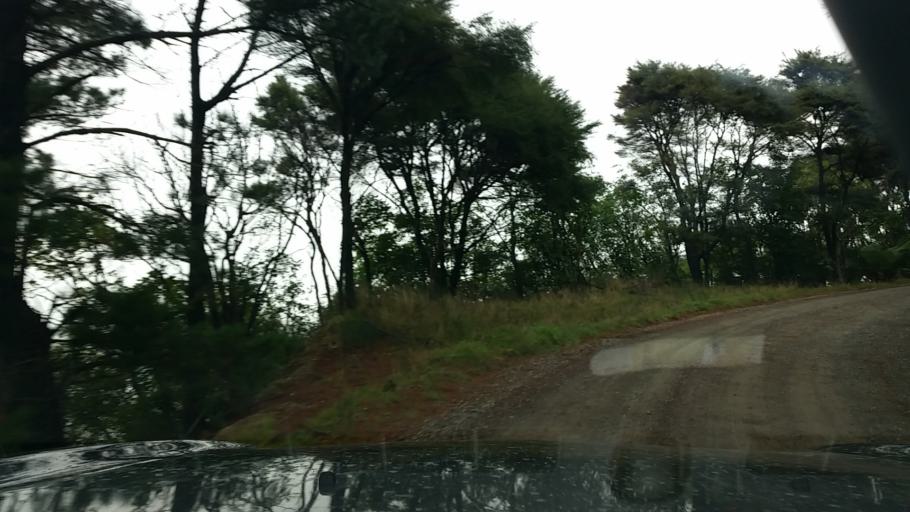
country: NZ
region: Marlborough
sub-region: Marlborough District
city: Picton
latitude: -41.1691
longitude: 174.0206
